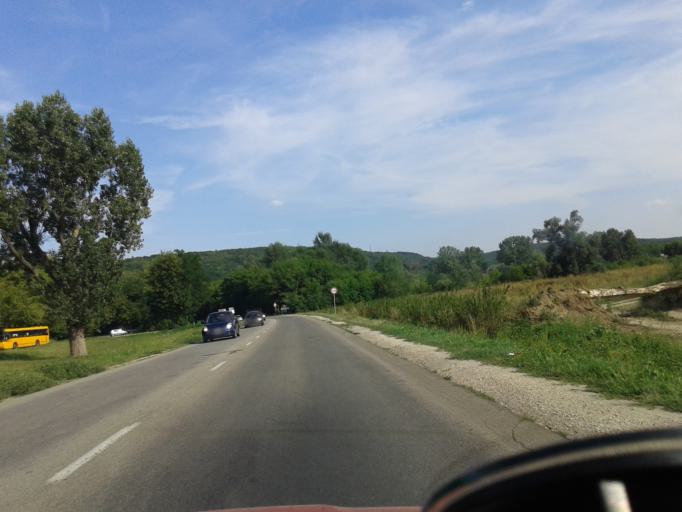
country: HU
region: Pest
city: Godollo
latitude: 47.5975
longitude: 19.3946
